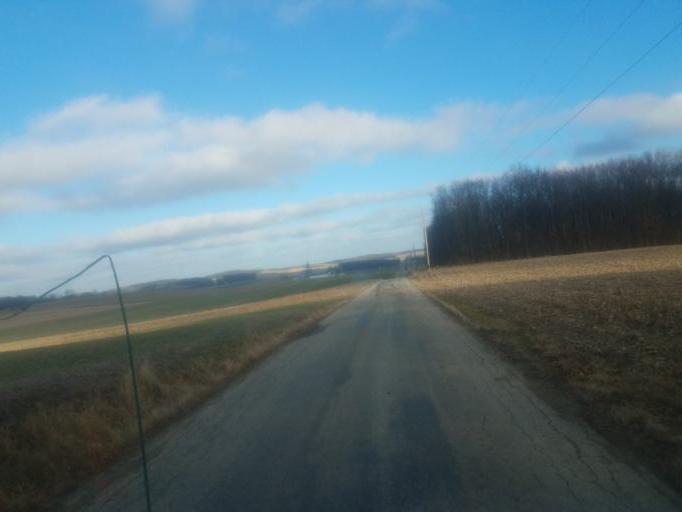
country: US
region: Ohio
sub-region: Ashland County
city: Loudonville
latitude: 40.6090
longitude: -82.3688
